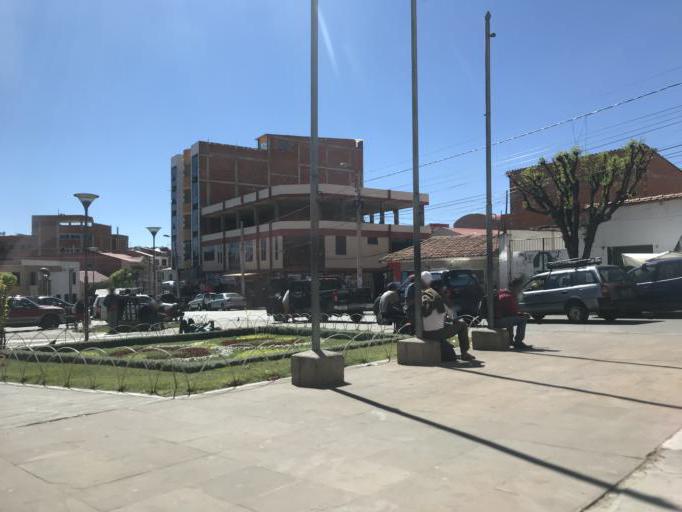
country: BO
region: Chuquisaca
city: Sucre
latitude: -19.0366
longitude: -65.2555
